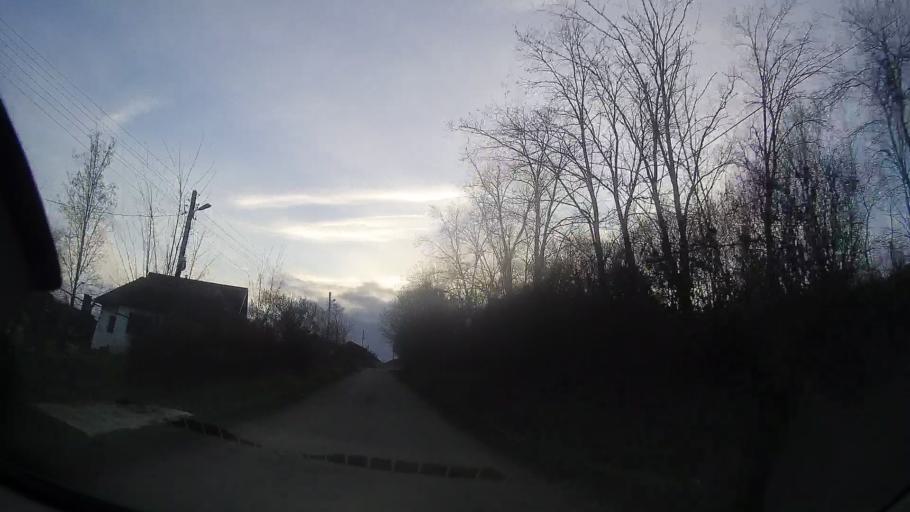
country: RO
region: Cluj
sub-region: Comuna Geaca
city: Geaca
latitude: 46.8562
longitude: 24.0862
